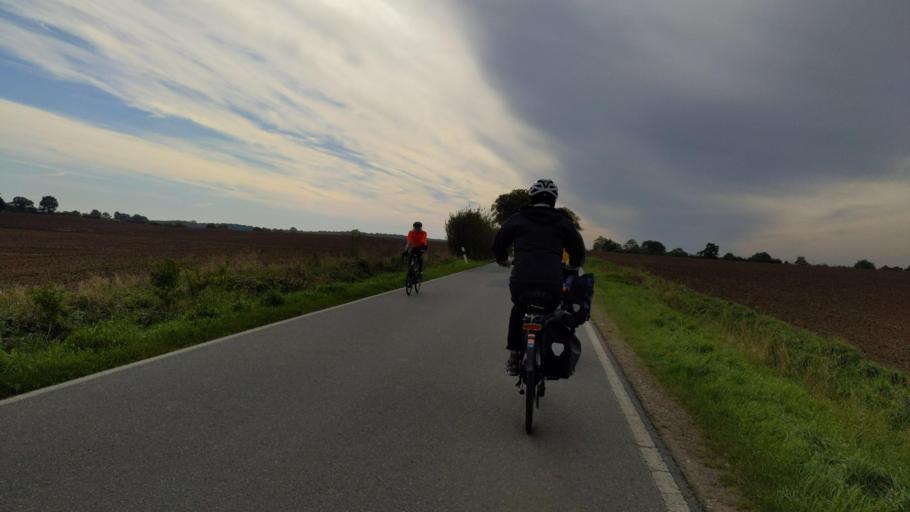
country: DE
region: Schleswig-Holstein
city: Rehhorst
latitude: 53.8838
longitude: 10.4760
